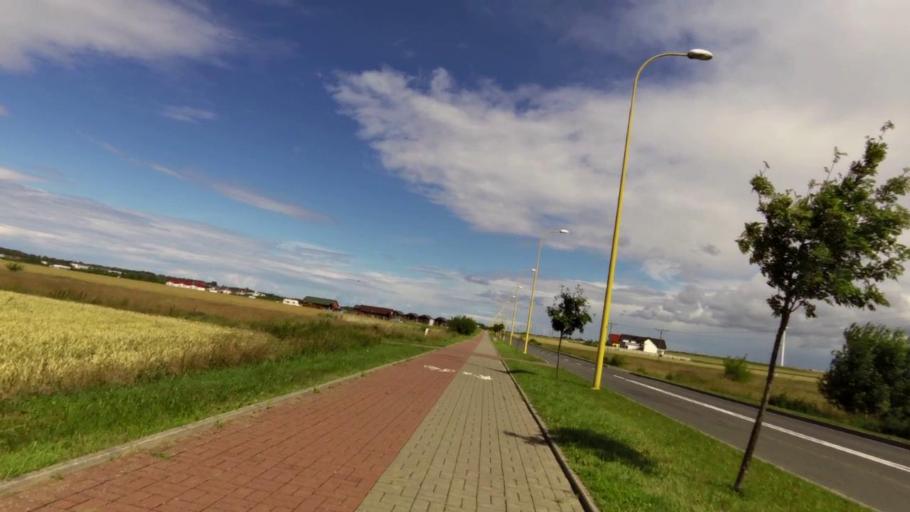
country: PL
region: West Pomeranian Voivodeship
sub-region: Powiat slawienski
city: Darlowo
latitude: 54.4351
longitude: 16.4105
